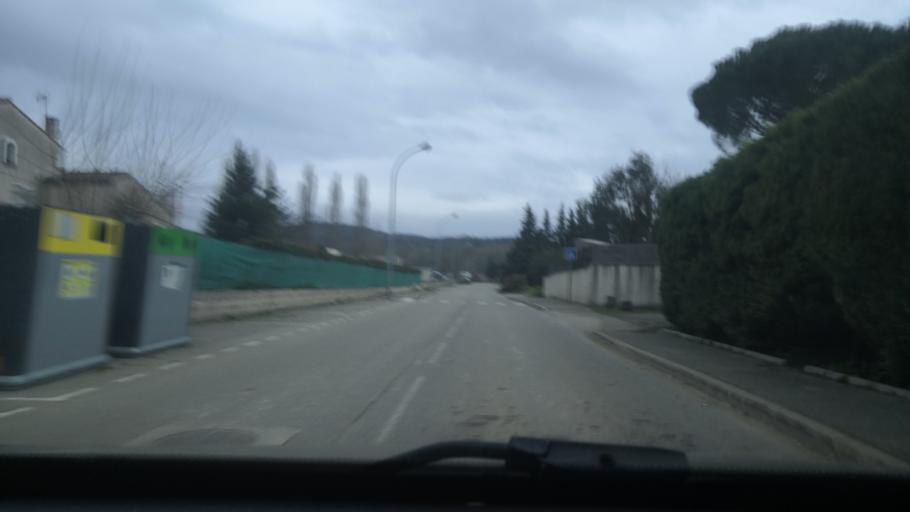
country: FR
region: Rhone-Alpes
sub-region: Departement de la Drome
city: Montboucher-sur-Jabron
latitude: 44.5477
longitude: 4.7935
